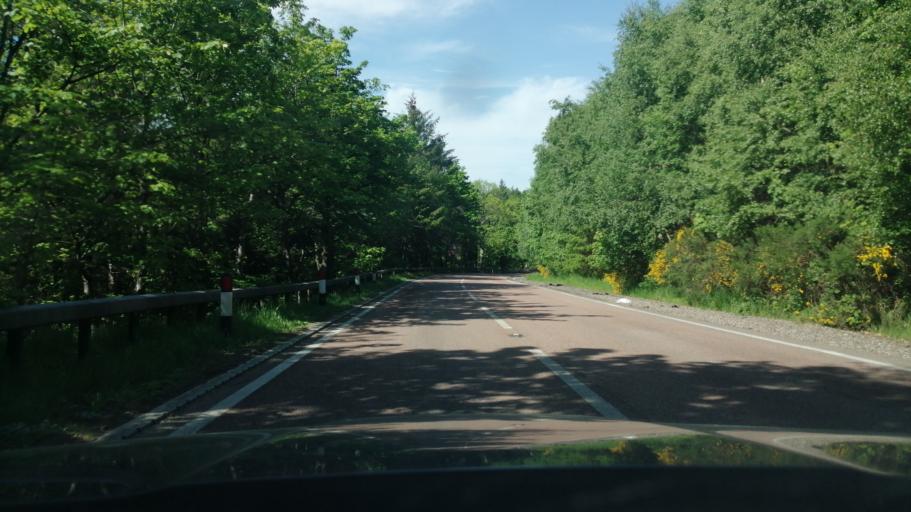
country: GB
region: Scotland
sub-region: Moray
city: Rothes
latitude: 57.4884
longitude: -3.1762
